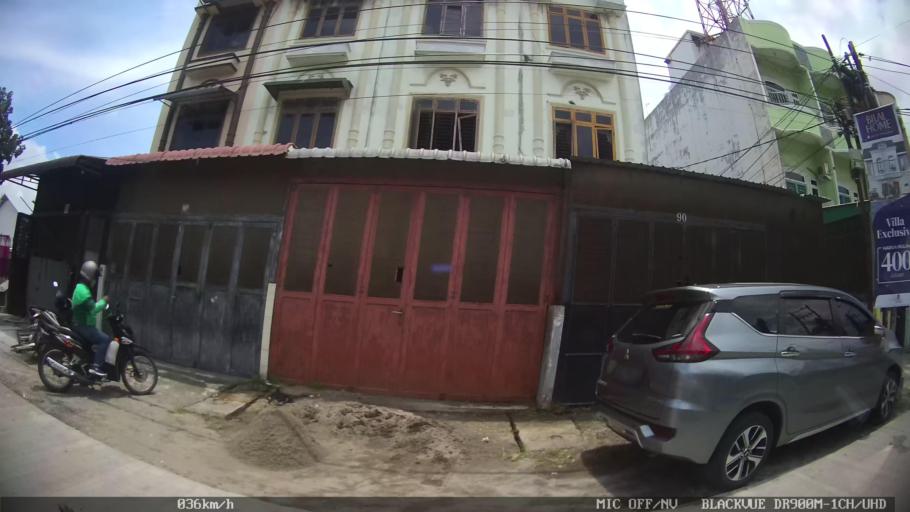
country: ID
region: North Sumatra
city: Medan
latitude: 3.6260
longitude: 98.6801
